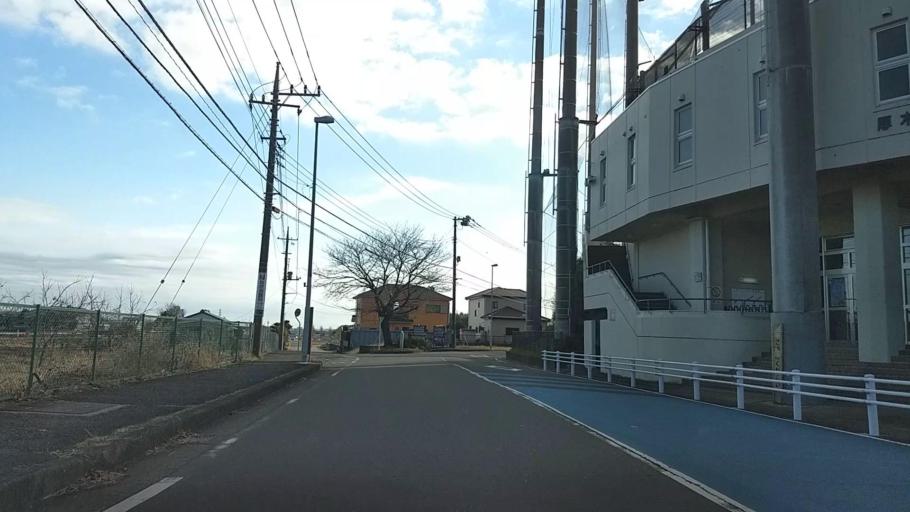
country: JP
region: Kanagawa
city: Atsugi
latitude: 35.4315
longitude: 139.3234
